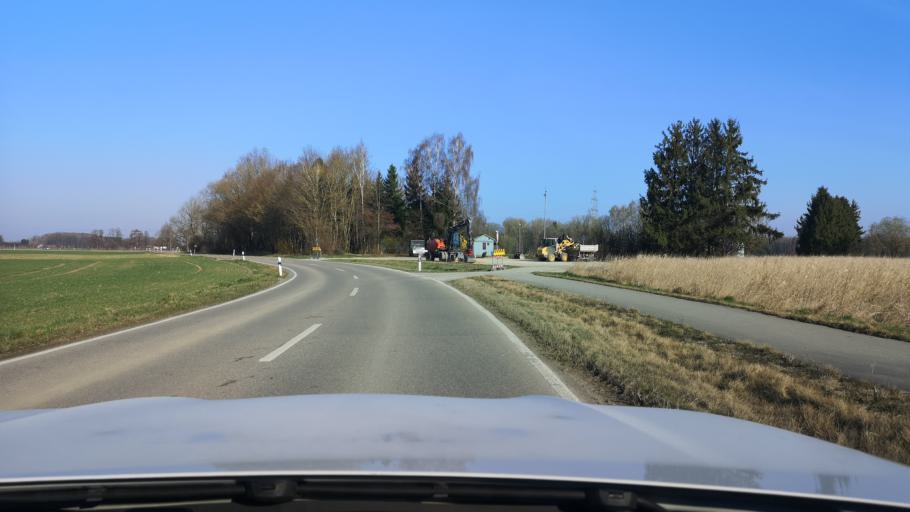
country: DE
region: Bavaria
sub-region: Upper Bavaria
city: Markt Schwaben
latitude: 48.2002
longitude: 11.8562
